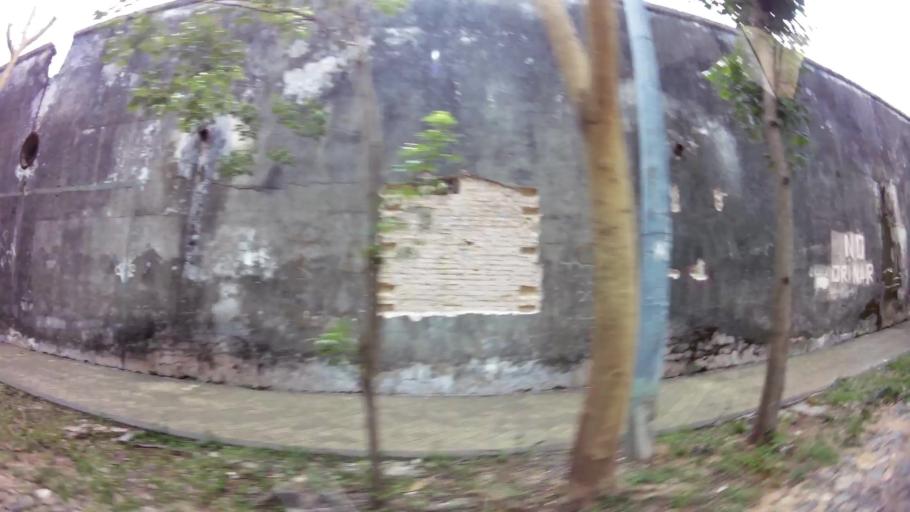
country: PY
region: Asuncion
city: Asuncion
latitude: -25.2896
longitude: -57.5817
